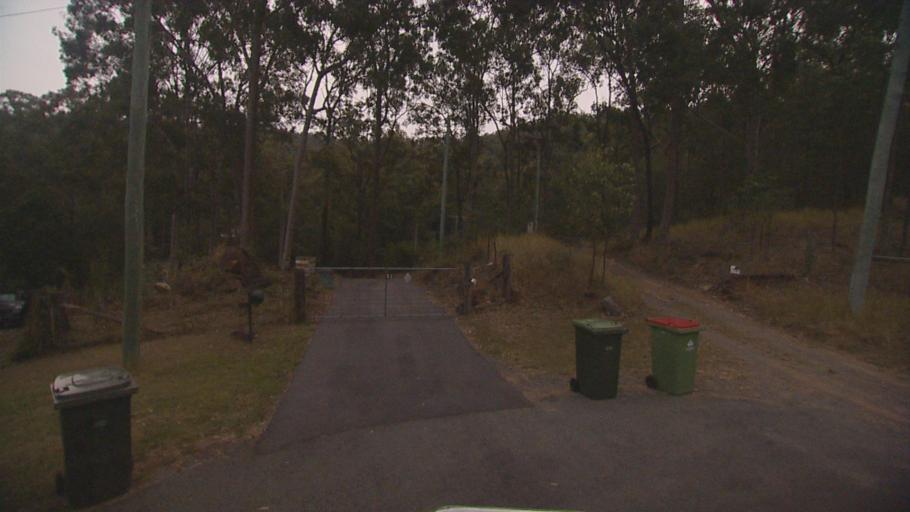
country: AU
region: Queensland
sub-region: Logan
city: Chambers Flat
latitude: -27.8213
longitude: 153.0909
